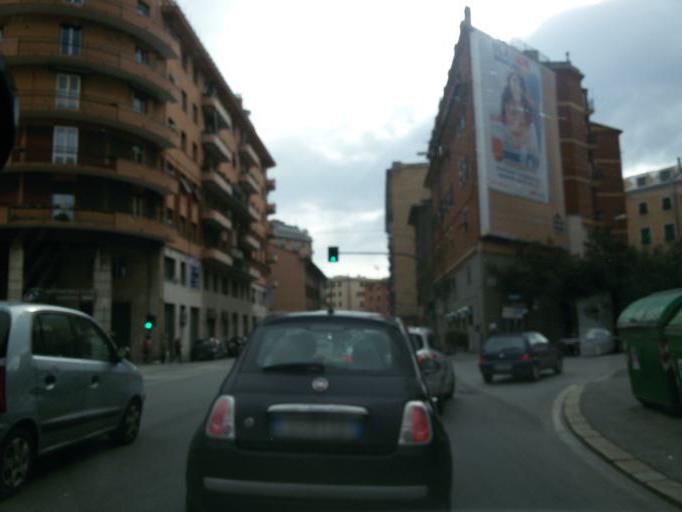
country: IT
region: Liguria
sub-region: Provincia di Genova
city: San Teodoro
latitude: 44.4122
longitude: 8.8849
